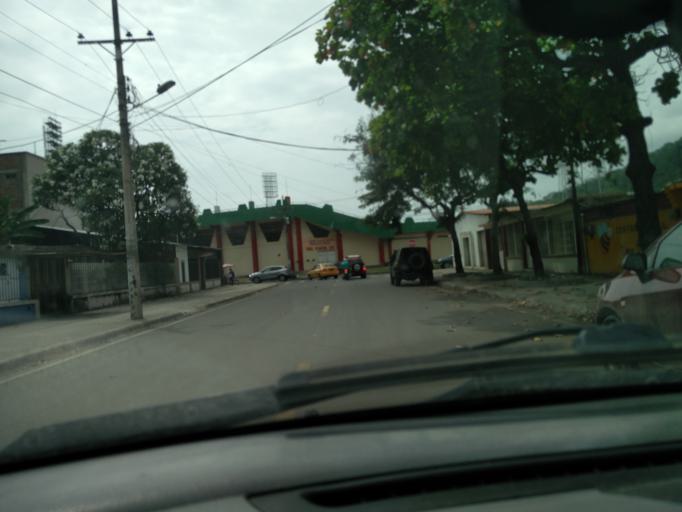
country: EC
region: Manabi
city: Portoviejo
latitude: -1.0501
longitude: -80.4532
